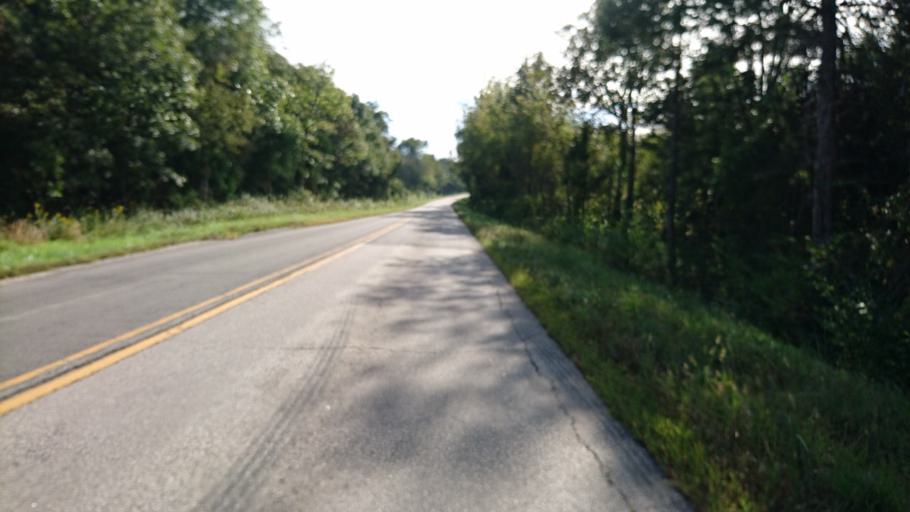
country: US
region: Missouri
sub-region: Crawford County
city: Cuba
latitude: 38.1016
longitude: -91.3496
